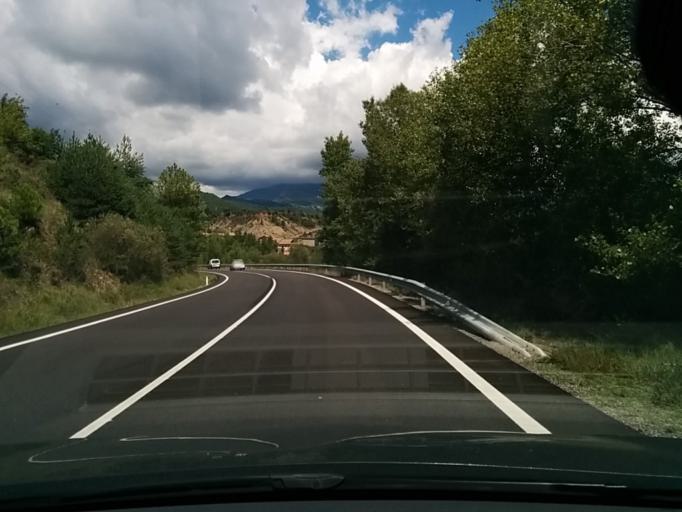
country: ES
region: Aragon
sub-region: Provincia de Huesca
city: Laspuna
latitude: 42.4948
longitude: 0.1458
